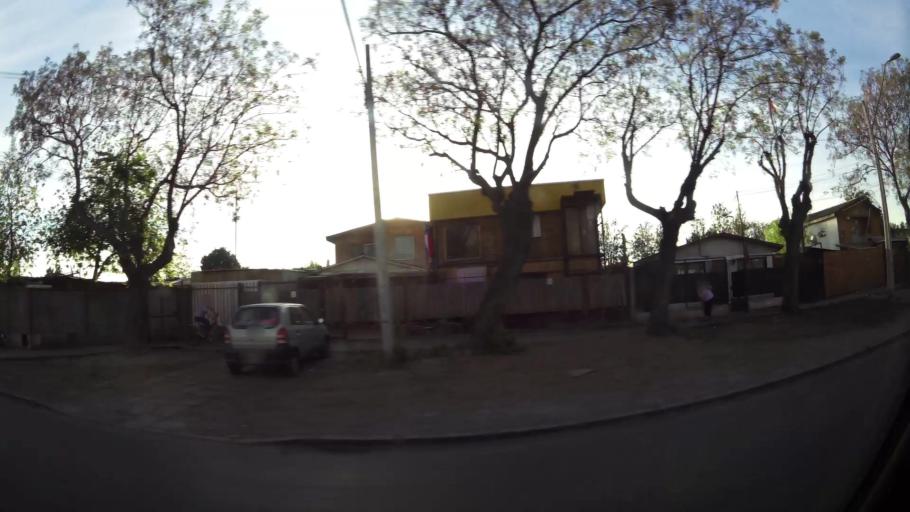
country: CL
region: Santiago Metropolitan
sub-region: Provincia de Santiago
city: Lo Prado
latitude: -33.4170
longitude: -70.7168
